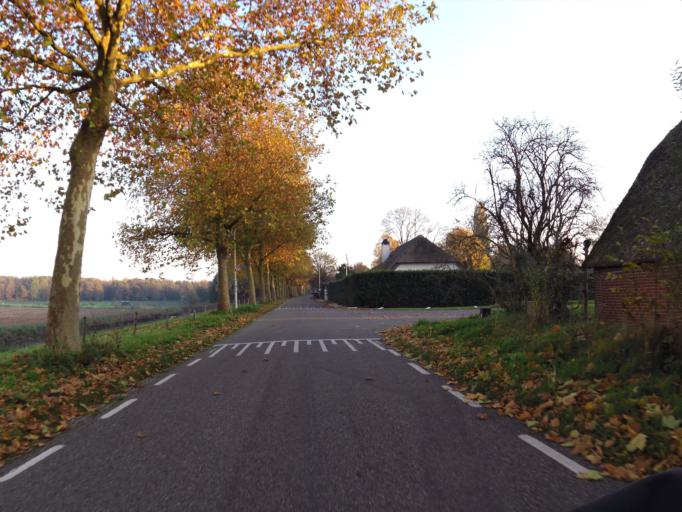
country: NL
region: Gelderland
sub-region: Gemeente Maasdriel
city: Hedel
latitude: 51.7050
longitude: 5.2306
